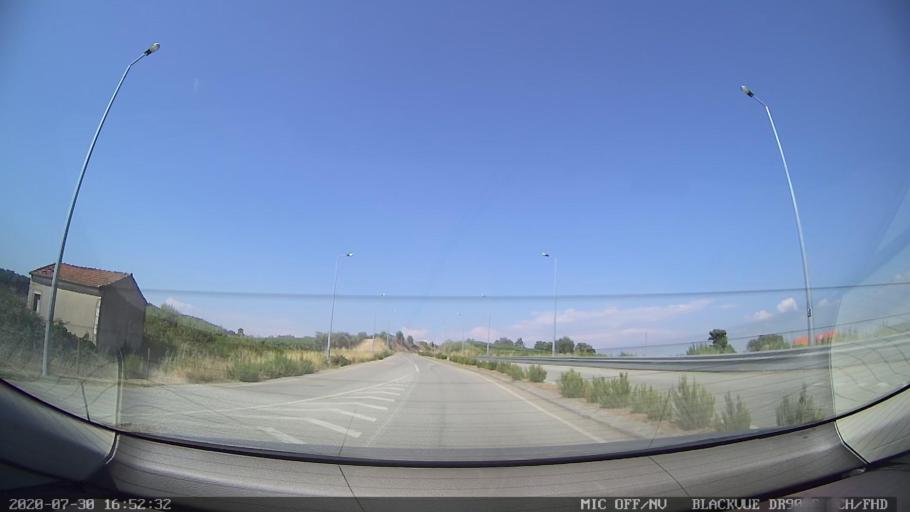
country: PT
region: Vila Real
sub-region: Sabrosa
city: Sabrosa
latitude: 41.2623
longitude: -7.4966
